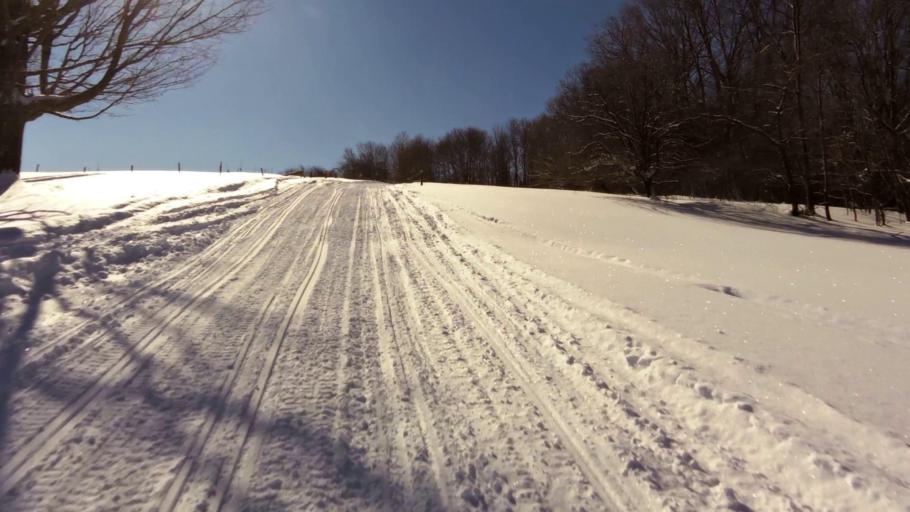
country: US
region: New York
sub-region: Chautauqua County
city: Fredonia
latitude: 42.3550
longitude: -79.1885
